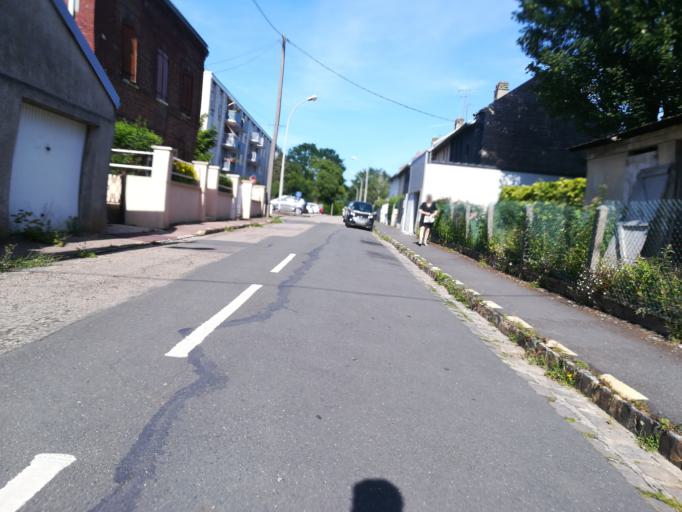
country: FR
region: Haute-Normandie
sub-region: Departement de la Seine-Maritime
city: Mont-Saint-Aignan
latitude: 49.4600
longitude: 1.0803
